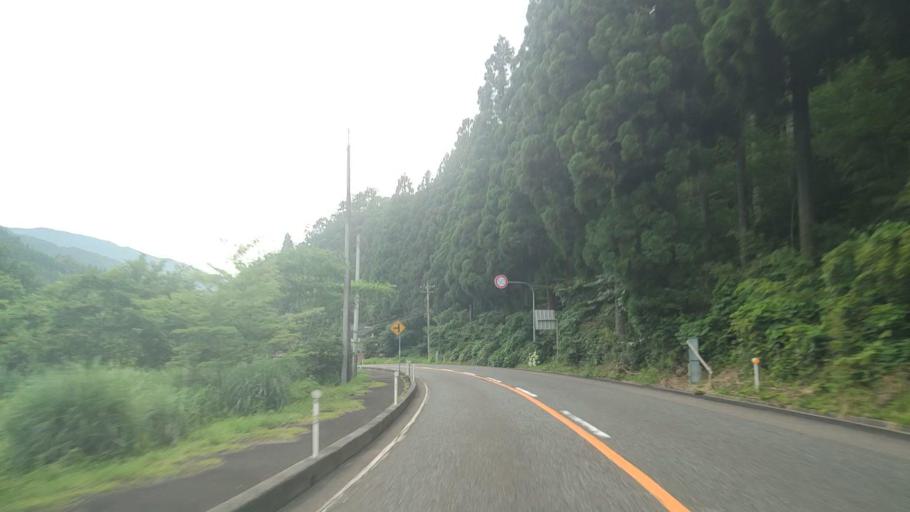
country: JP
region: Tottori
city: Kurayoshi
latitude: 35.3181
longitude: 133.8951
